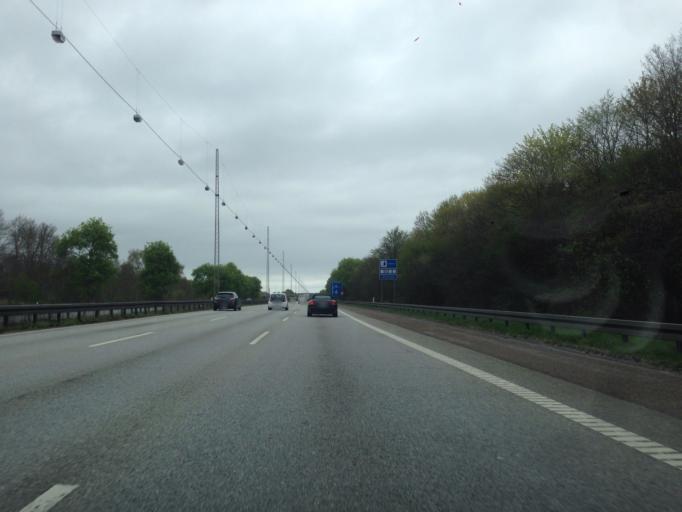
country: DK
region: Capital Region
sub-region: Lyngby-Tarbaek Kommune
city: Kongens Lyngby
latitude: 55.7823
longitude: 12.5272
